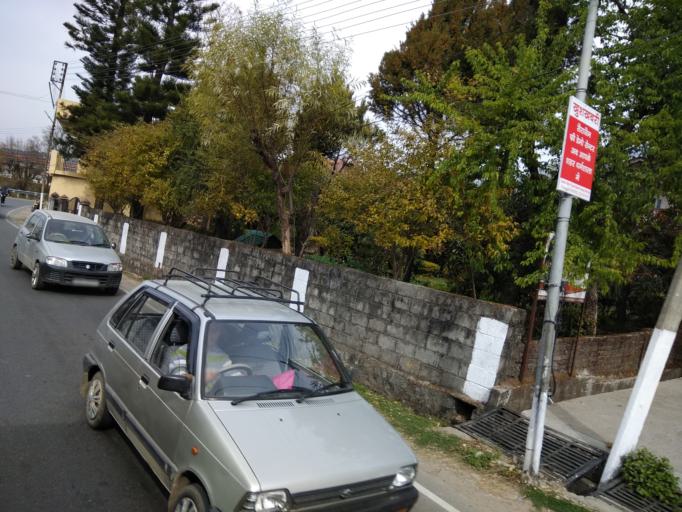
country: IN
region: Himachal Pradesh
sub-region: Kangra
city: Dharmsala
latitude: 32.1941
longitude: 76.3463
